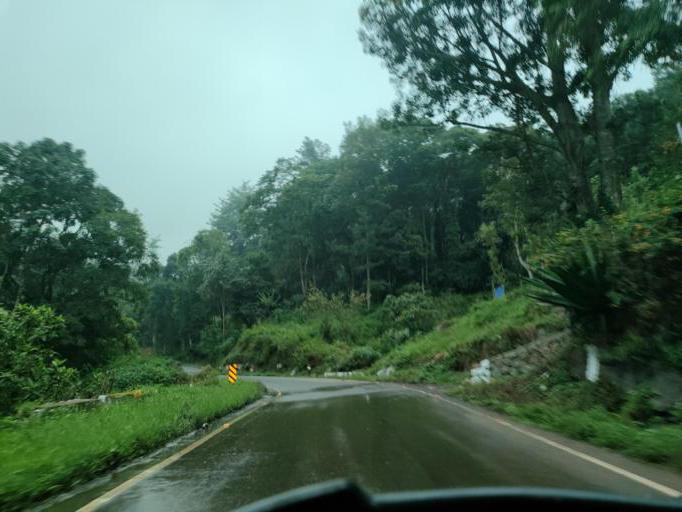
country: IN
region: Tamil Nadu
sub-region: Dindigul
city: Ayakudi
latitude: 10.3537
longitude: 77.5610
